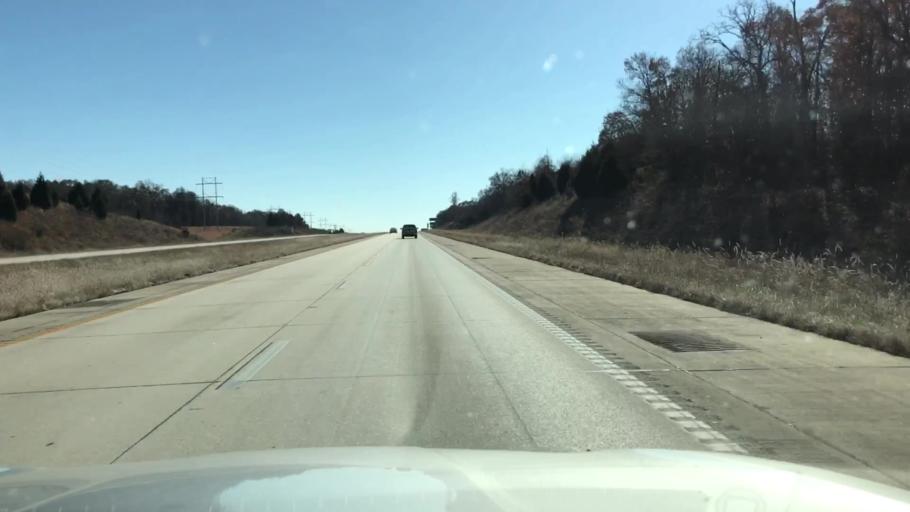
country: US
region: Missouri
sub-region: Jasper County
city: Duquesne
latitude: 37.0141
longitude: -94.4306
